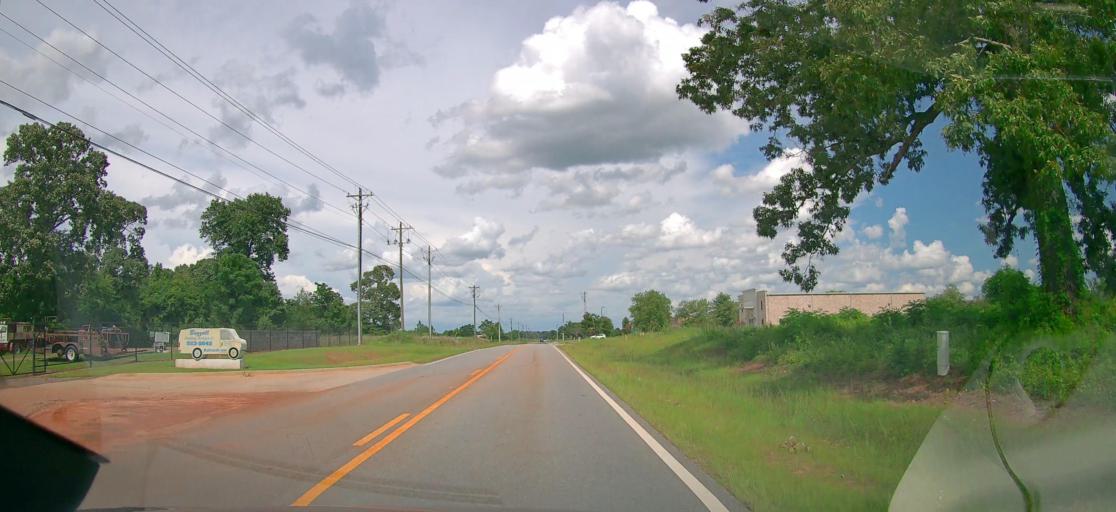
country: US
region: Georgia
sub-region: Houston County
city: Centerville
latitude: 32.5784
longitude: -83.7102
